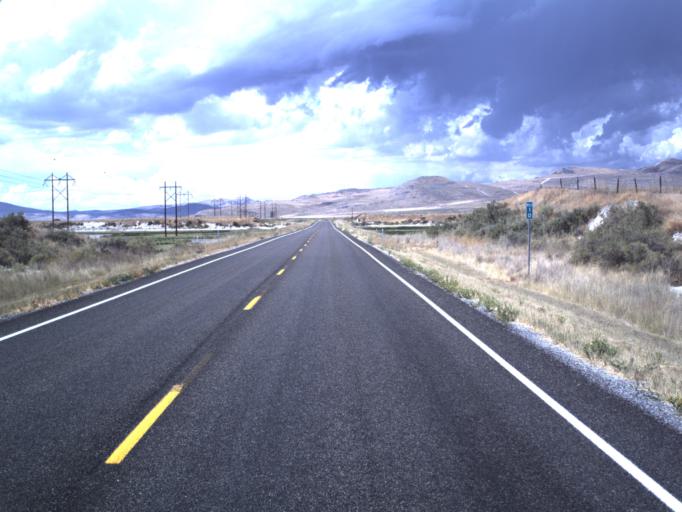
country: US
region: Utah
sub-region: Box Elder County
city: Tremonton
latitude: 41.6022
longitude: -112.3090
